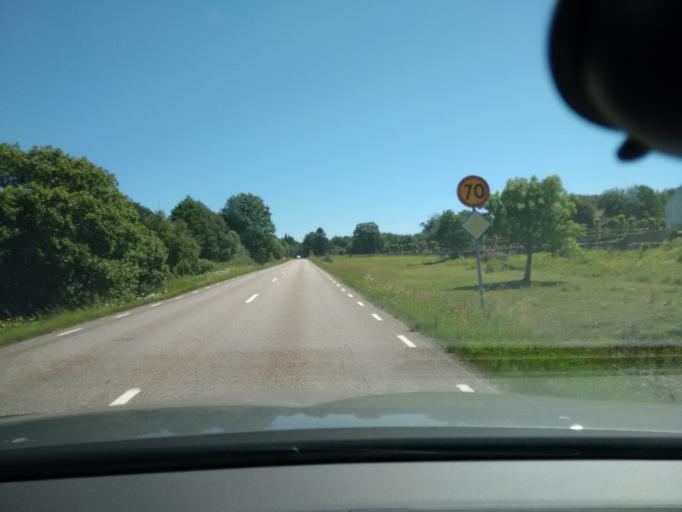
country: SE
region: Skane
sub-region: Horby Kommun
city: Hoerby
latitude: 55.7884
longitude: 13.8386
